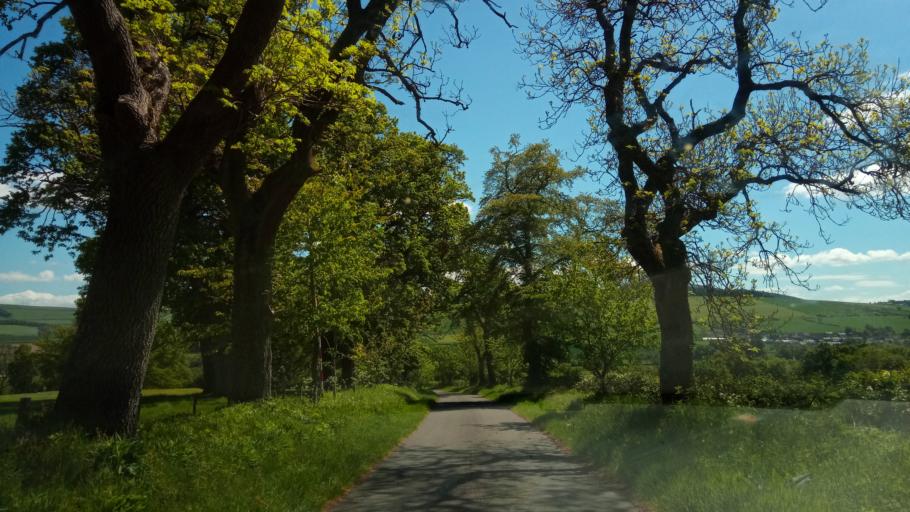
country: GB
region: Scotland
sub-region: The Scottish Borders
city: Saint Boswells
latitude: 55.4708
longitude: -2.6830
